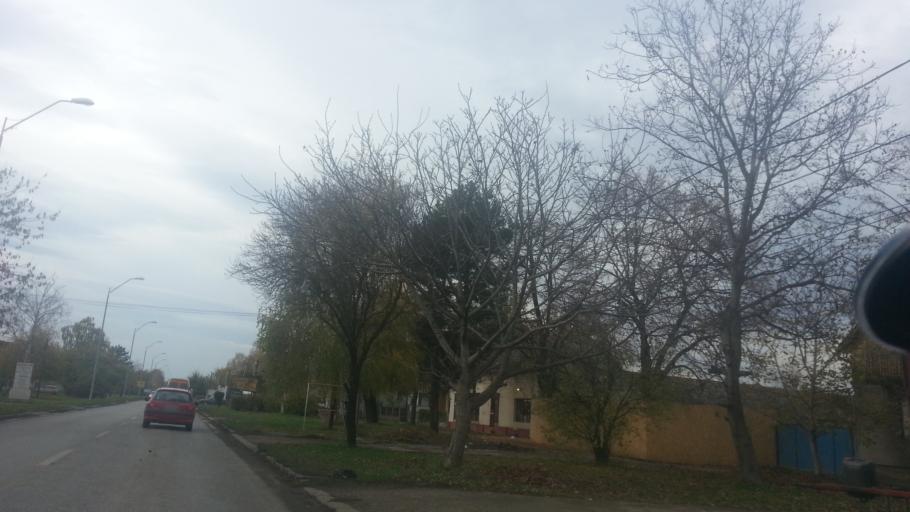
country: RS
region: Autonomna Pokrajina Vojvodina
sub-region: Sremski Okrug
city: Stara Pazova
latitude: 44.9842
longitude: 20.1540
